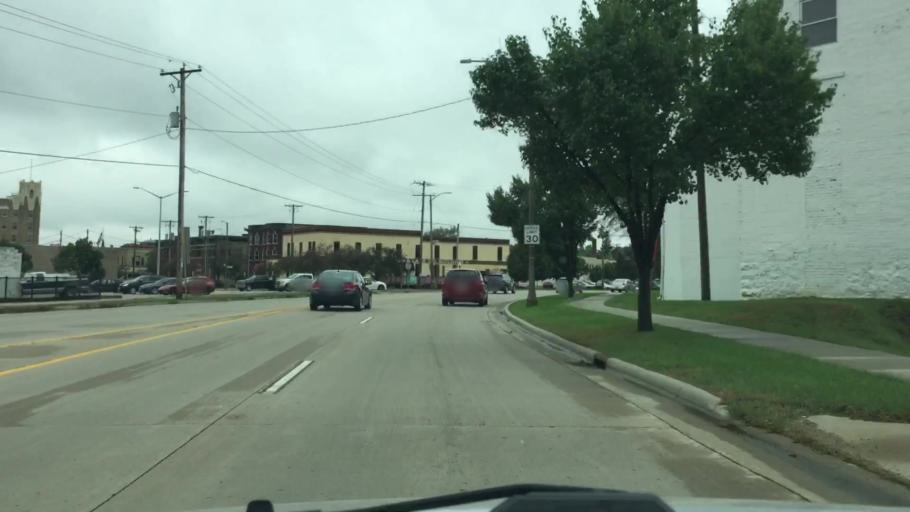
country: US
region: Wisconsin
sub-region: Rock County
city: Janesville
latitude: 42.6829
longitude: -89.0288
